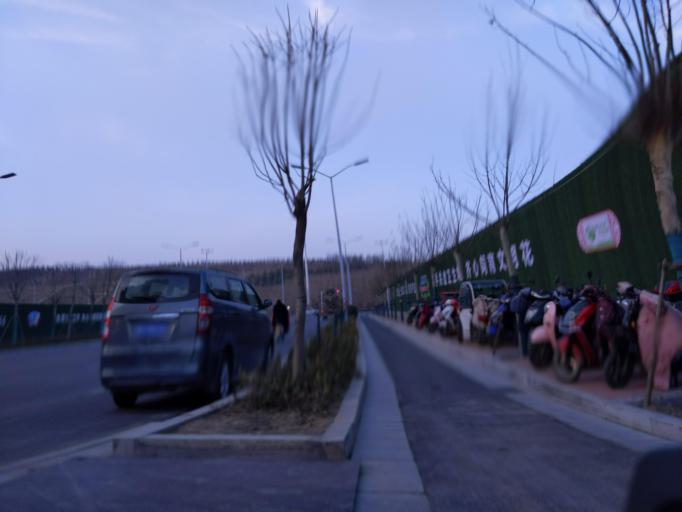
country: CN
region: Henan Sheng
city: Puyang
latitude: 35.8167
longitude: 115.0118
